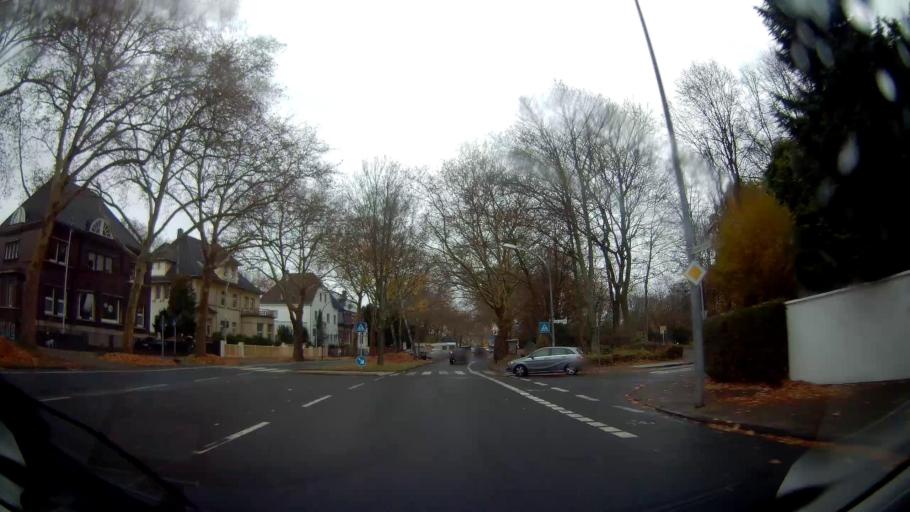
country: DE
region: North Rhine-Westphalia
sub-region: Regierungsbezirk Munster
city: Gelsenkirchen
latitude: 51.4933
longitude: 7.0828
